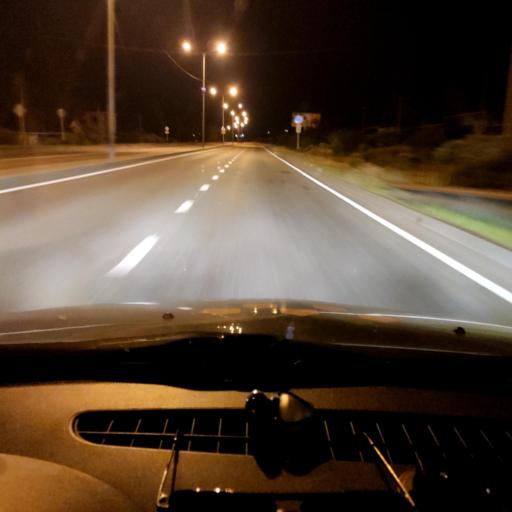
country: RU
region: Belgorod
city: Gubkin
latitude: 51.2706
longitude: 37.5763
